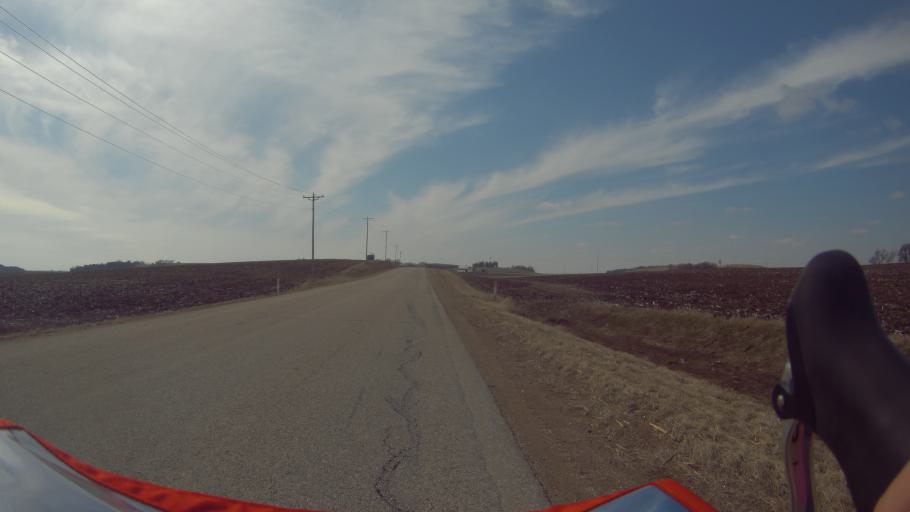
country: US
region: Wisconsin
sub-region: Dane County
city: Waunakee
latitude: 43.1626
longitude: -89.4939
